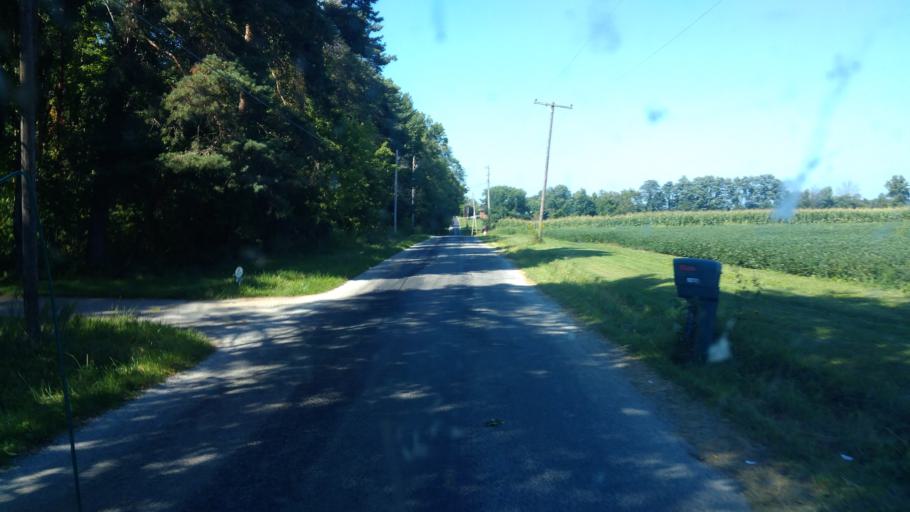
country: US
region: Ohio
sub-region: Ashland County
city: Ashland
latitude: 40.9061
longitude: -82.2623
